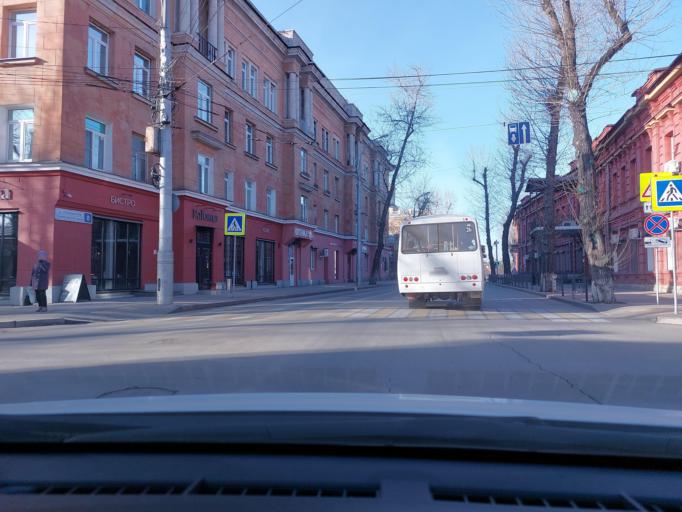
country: RU
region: Irkutsk
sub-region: Irkutskiy Rayon
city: Irkutsk
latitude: 52.2849
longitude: 104.2835
